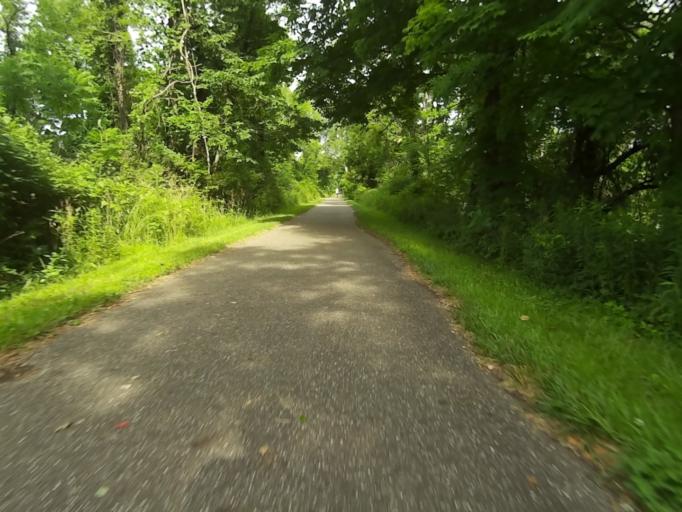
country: US
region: Ohio
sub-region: Portage County
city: Kent
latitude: 41.1852
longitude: -81.3684
